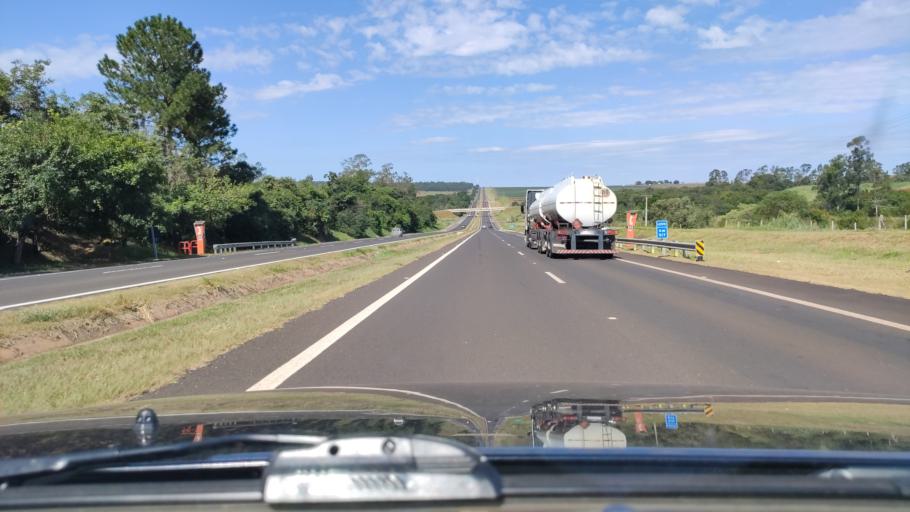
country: BR
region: Sao Paulo
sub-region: Rancharia
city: Rancharia
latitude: -22.4120
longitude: -51.0486
